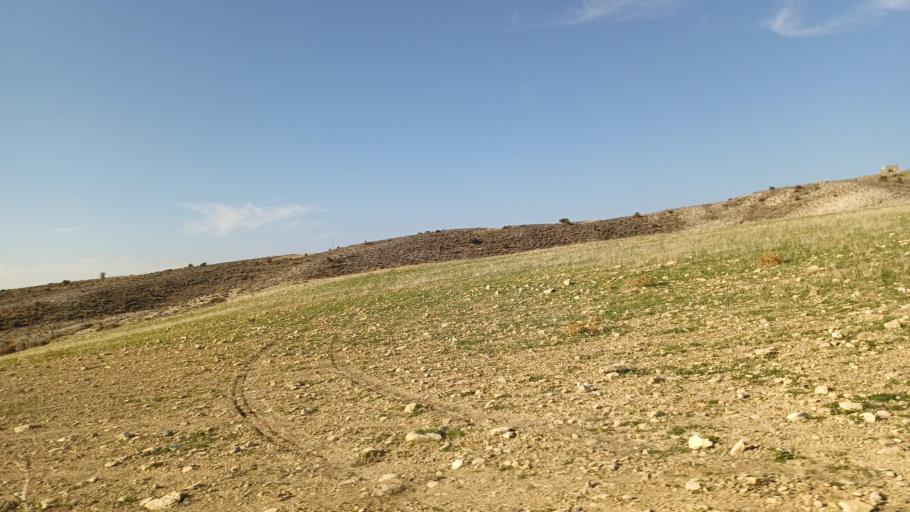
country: CY
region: Larnaka
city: Psevdas
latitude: 34.9452
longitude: 33.5181
